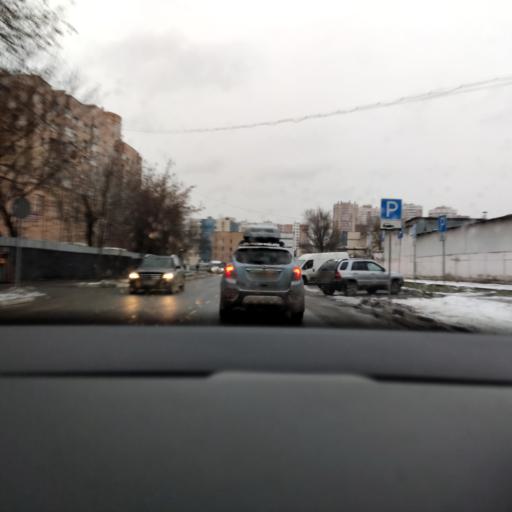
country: RU
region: Moskovskaya
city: Reutov
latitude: 55.7553
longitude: 37.8626
